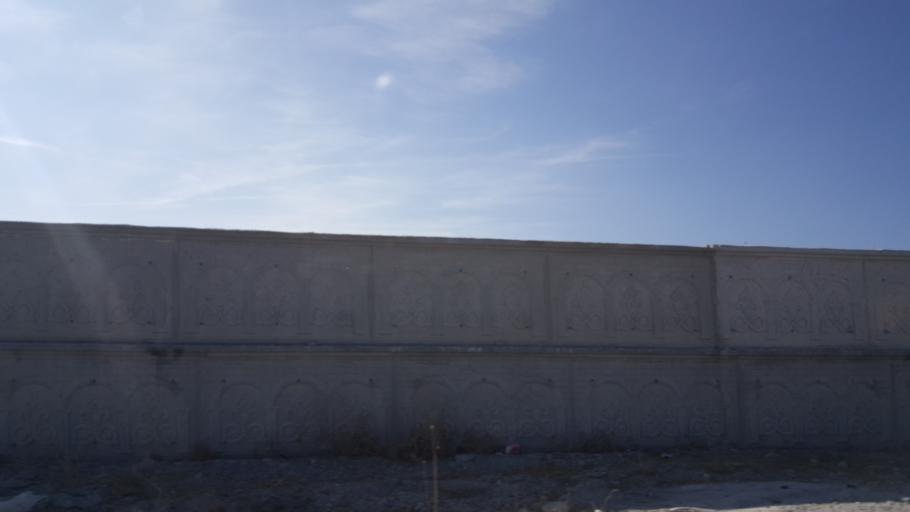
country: TR
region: Ankara
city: Altpinar
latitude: 39.2336
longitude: 32.7425
